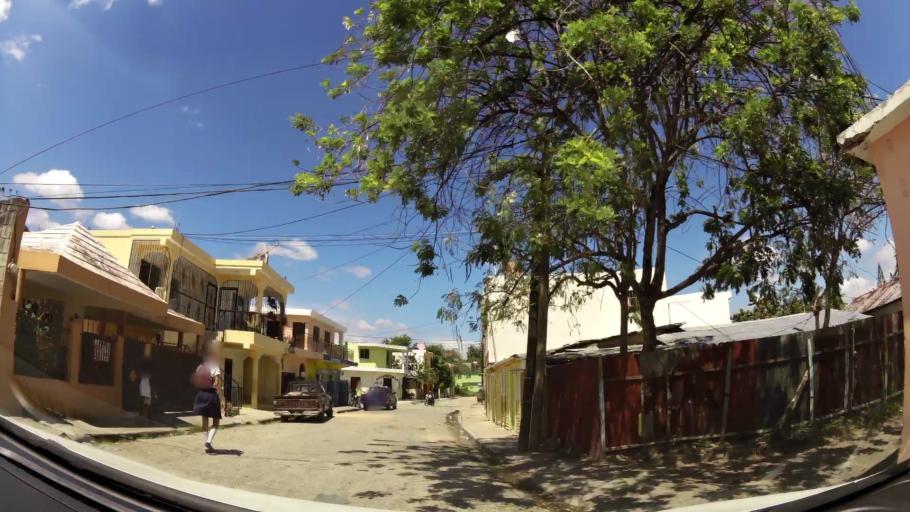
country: DO
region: San Cristobal
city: San Cristobal
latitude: 18.4050
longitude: -70.1094
